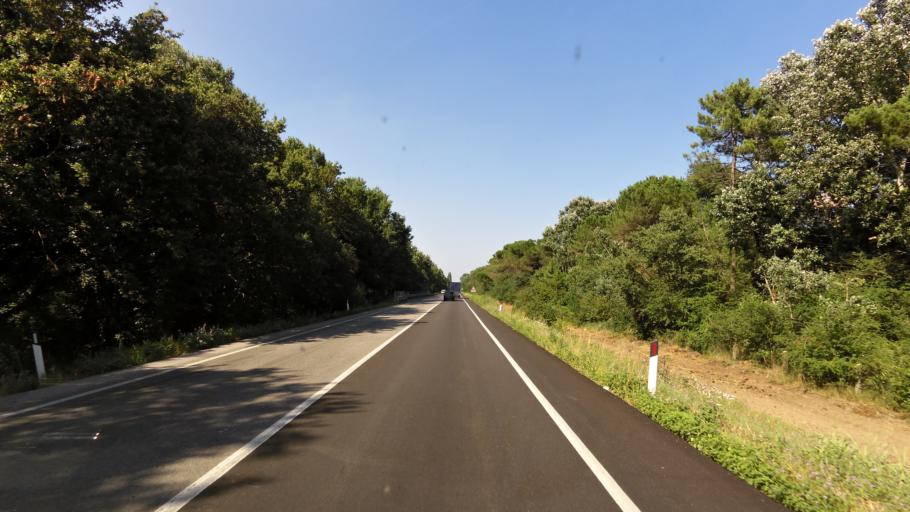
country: IT
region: Emilia-Romagna
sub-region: Provincia di Ravenna
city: Marina Romea
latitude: 44.5011
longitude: 12.2191
